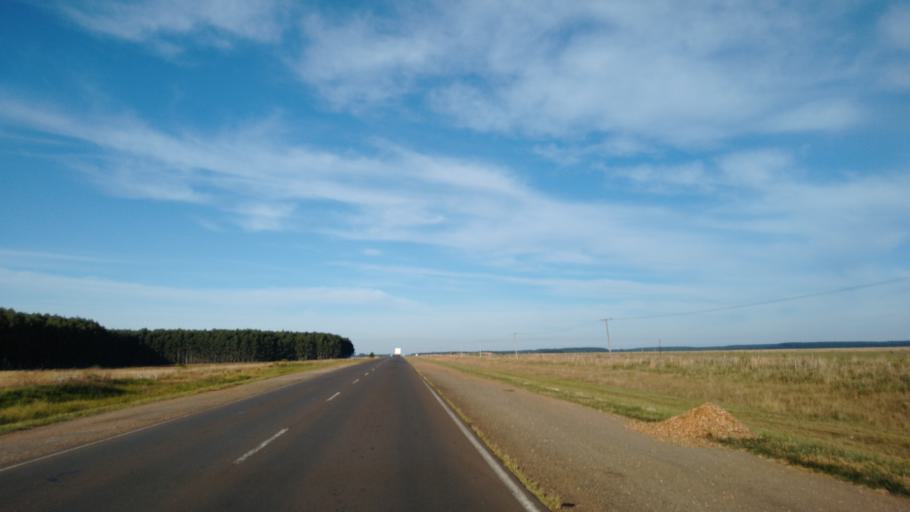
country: AR
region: Corrientes
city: Yapeyu
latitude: -29.3065
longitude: -56.7775
